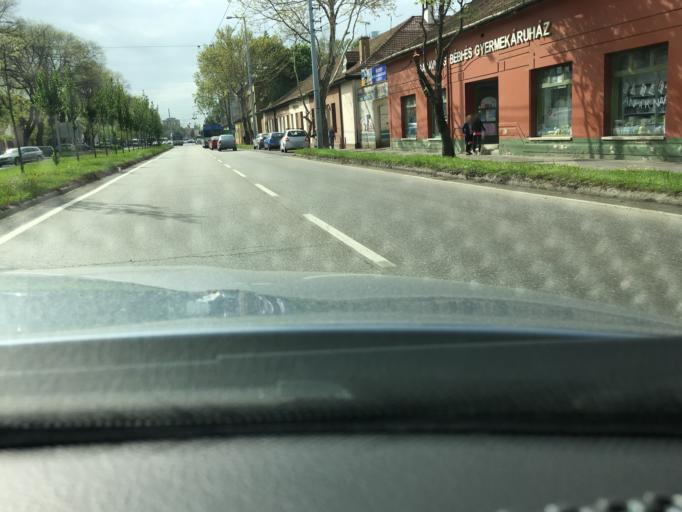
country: HU
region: Hajdu-Bihar
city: Debrecen
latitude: 47.5278
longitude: 21.6149
